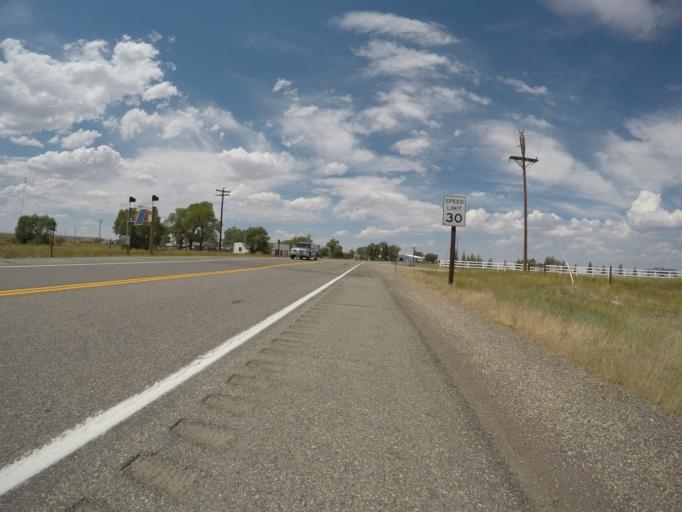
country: US
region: Wyoming
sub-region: Albany County
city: Laramie
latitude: 41.7365
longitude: -105.9745
